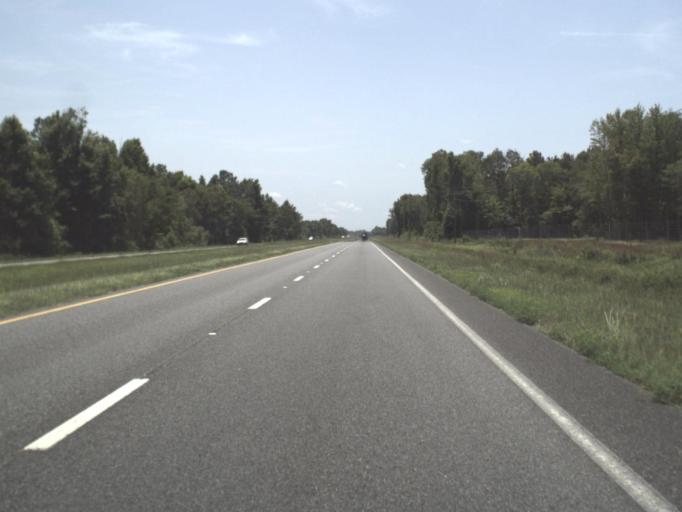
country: US
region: Florida
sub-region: Taylor County
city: Steinhatchee
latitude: 29.8372
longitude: -83.3676
